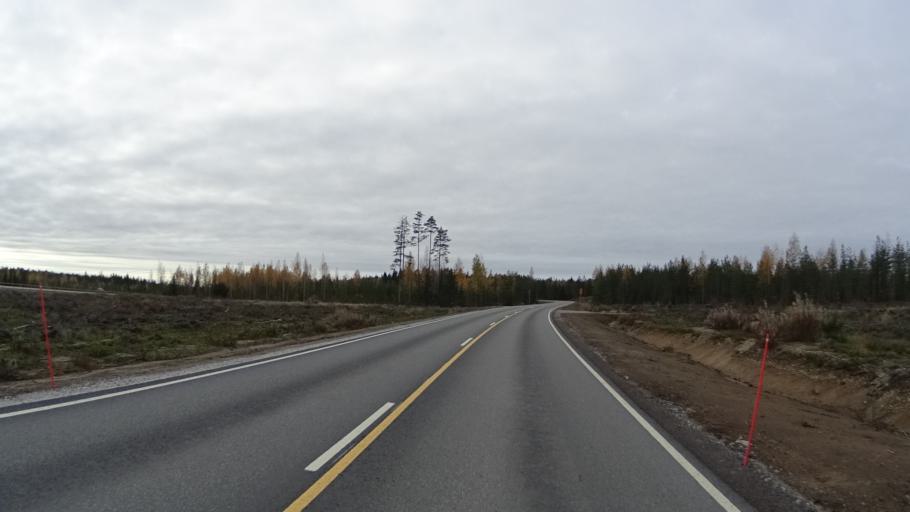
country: FI
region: South Karelia
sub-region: Lappeenranta
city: Lemi
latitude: 60.9965
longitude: 27.9312
